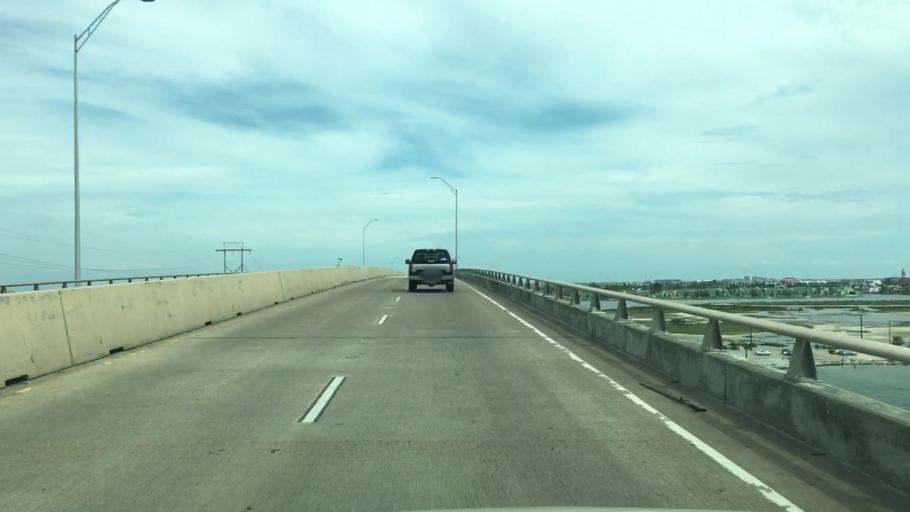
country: US
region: Texas
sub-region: Nueces County
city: Corpus Christi
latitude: 27.6353
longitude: -97.2411
